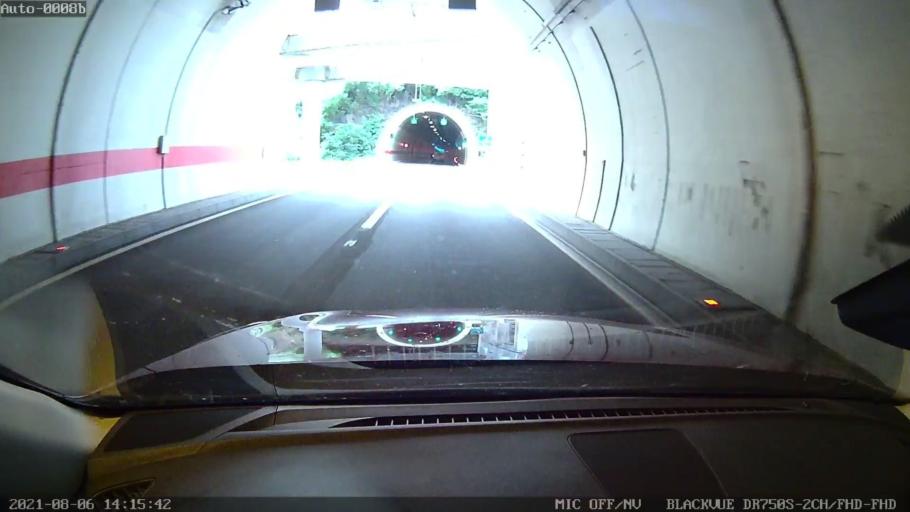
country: HR
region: Primorsko-Goranska
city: Vrbovsko
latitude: 45.3762
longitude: 14.9633
